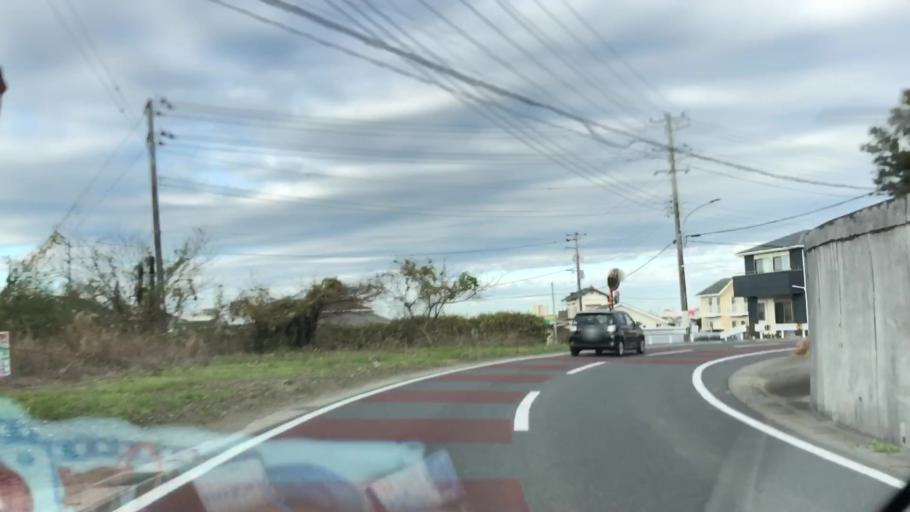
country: JP
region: Chiba
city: Tateyama
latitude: 35.0064
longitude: 139.8758
